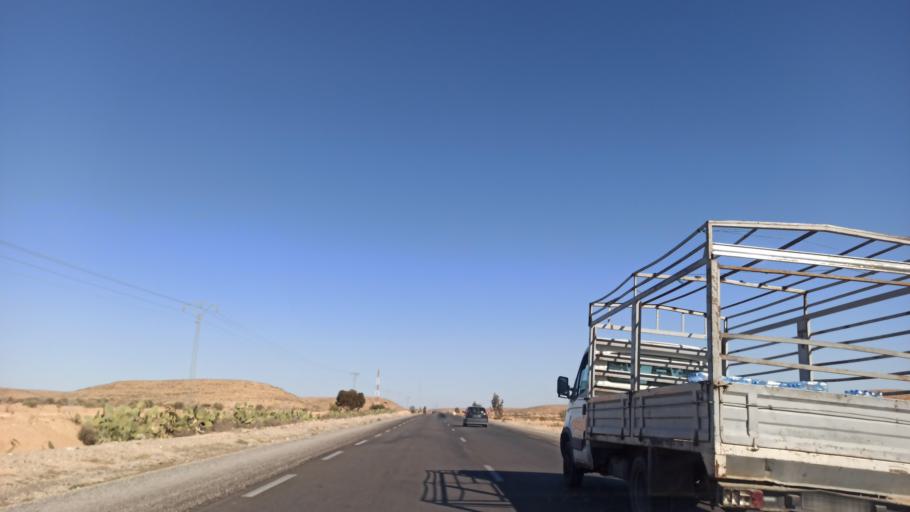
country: TN
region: Sidi Bu Zayd
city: Bi'r al Hufayy
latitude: 34.7115
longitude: 9.0507
